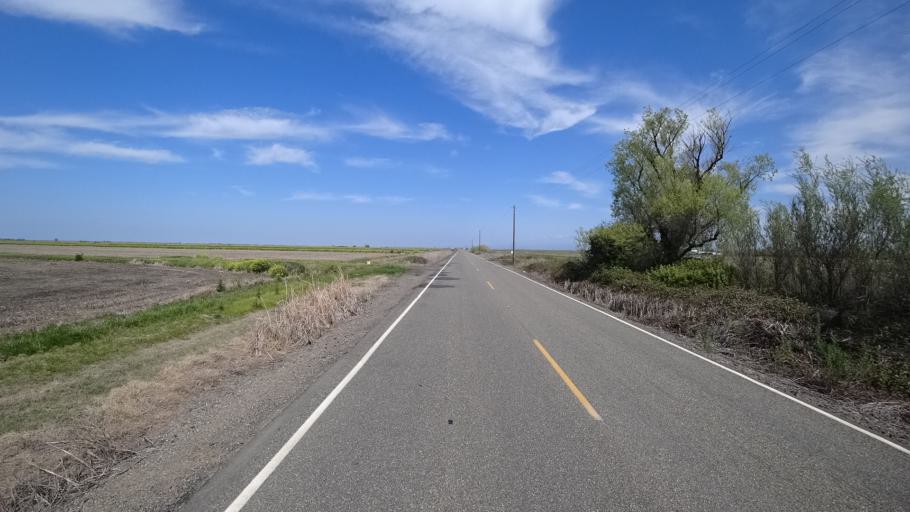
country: US
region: California
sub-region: Butte County
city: Durham
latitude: 39.5437
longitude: -121.8566
